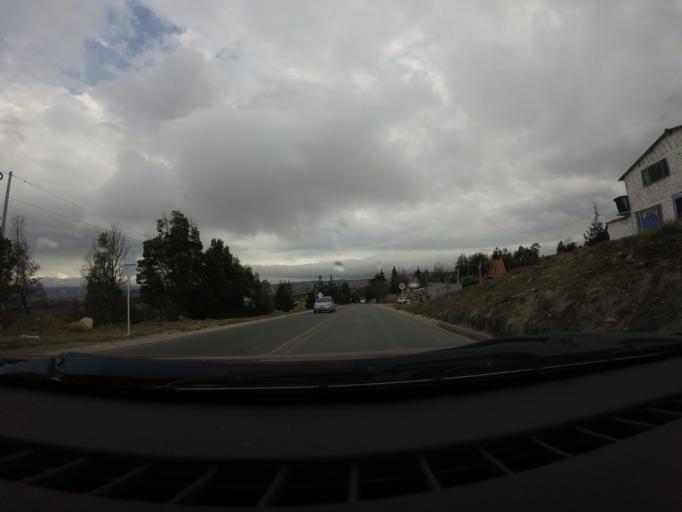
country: CO
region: Boyaca
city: Tunja
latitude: 5.5548
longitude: -73.4078
